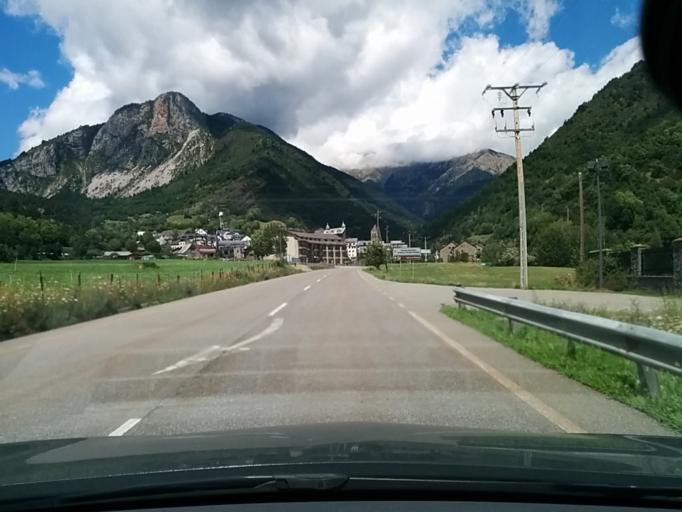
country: ES
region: Aragon
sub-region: Provincia de Huesca
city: Bielsa
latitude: 42.6298
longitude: 0.2230
